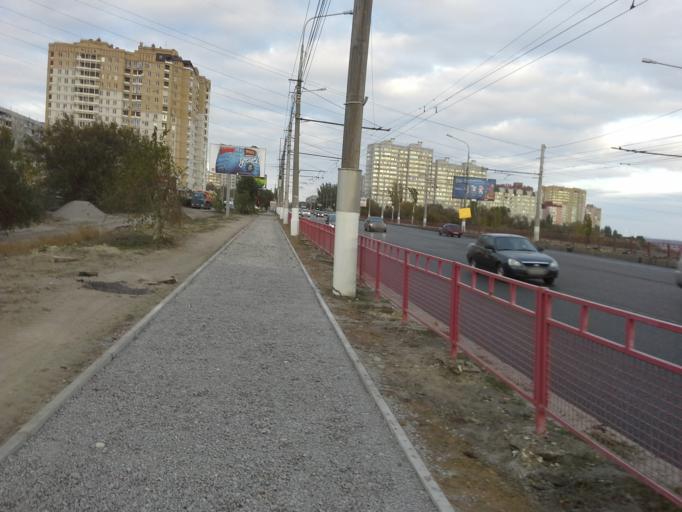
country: RU
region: Volgograd
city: Vodstroy
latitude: 48.8124
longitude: 44.6172
